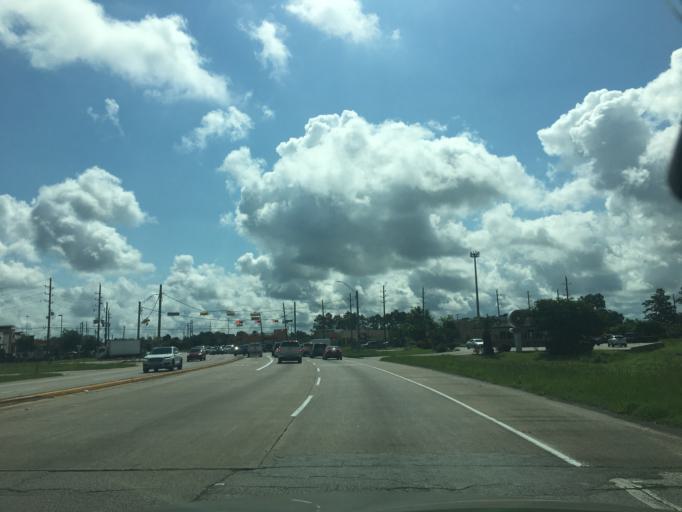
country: US
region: Texas
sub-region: Harris County
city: Spring
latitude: 30.0635
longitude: -95.4424
